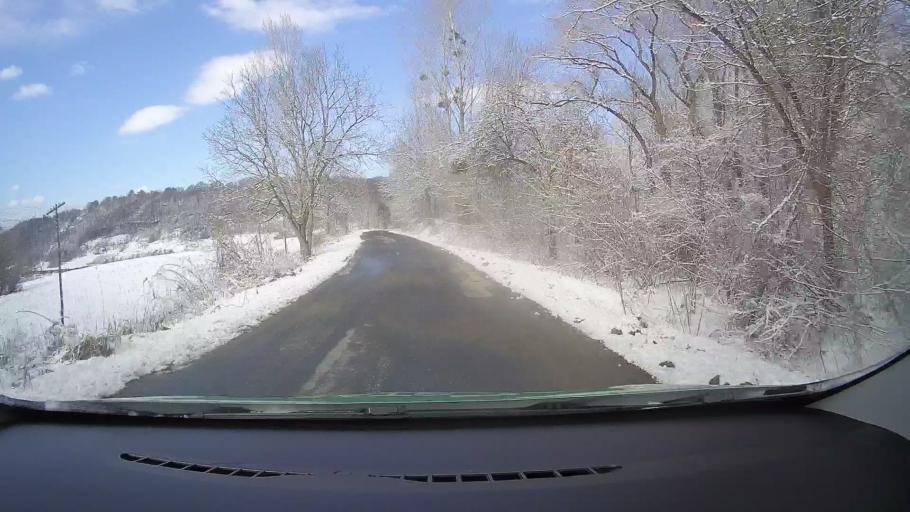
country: RO
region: Sibiu
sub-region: Comuna Mosna
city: Mosna
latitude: 46.0116
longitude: 24.4220
